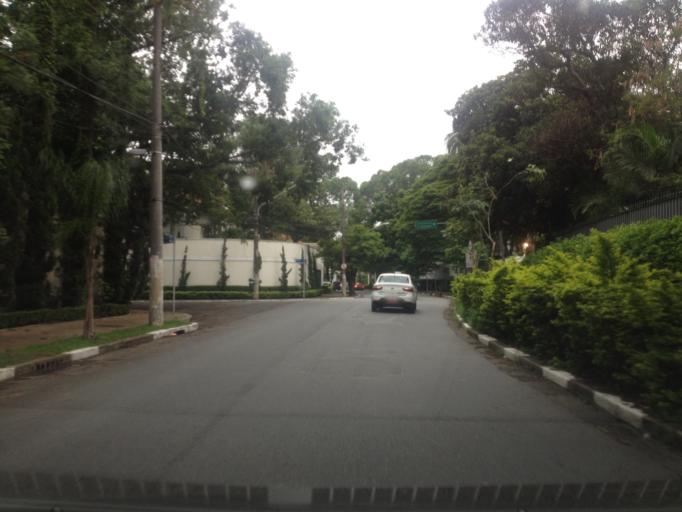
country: BR
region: Sao Paulo
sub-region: Sao Paulo
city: Sao Paulo
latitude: -23.5725
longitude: -46.6707
